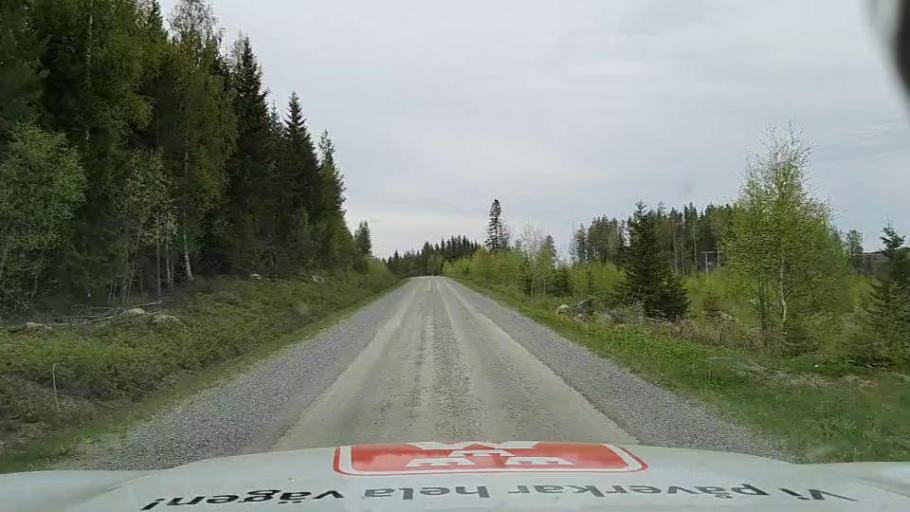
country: SE
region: Jaemtland
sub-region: OEstersunds Kommun
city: Brunflo
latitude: 62.6303
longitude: 14.9409
